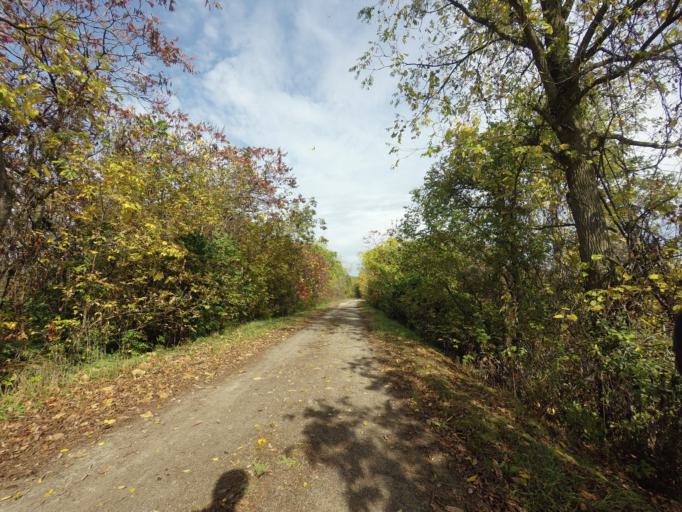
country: CA
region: Ontario
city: Brantford
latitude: 43.1624
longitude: -80.1830
